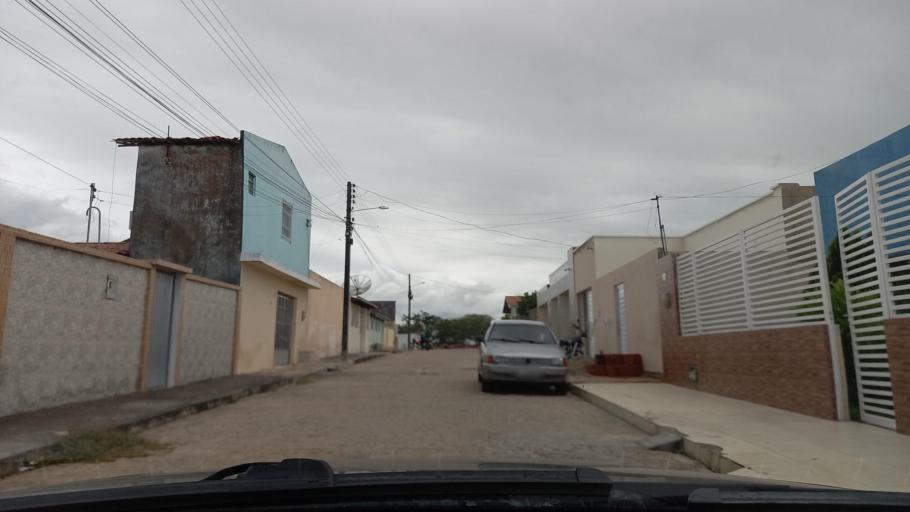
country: BR
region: Sergipe
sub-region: Caninde De Sao Francisco
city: Caninde de Sao Francisco
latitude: -9.6039
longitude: -37.7579
